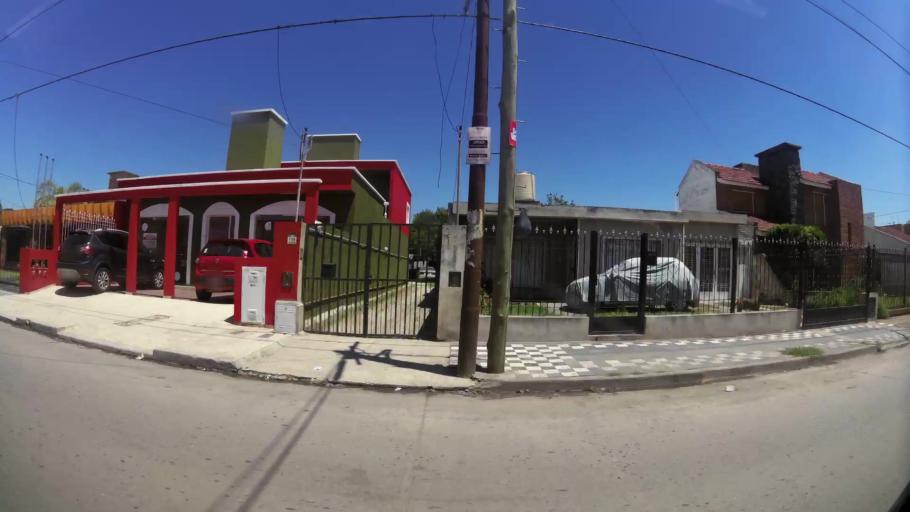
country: AR
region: Cordoba
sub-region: Departamento de Capital
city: Cordoba
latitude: -31.4140
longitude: -64.2313
